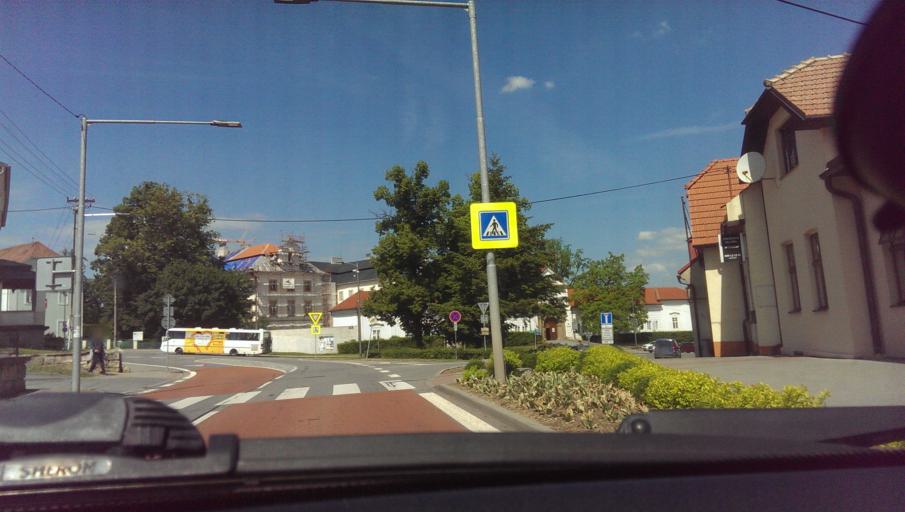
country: CZ
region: Zlin
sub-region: Okres Zlin
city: Vizovice
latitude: 49.2191
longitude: 17.8526
